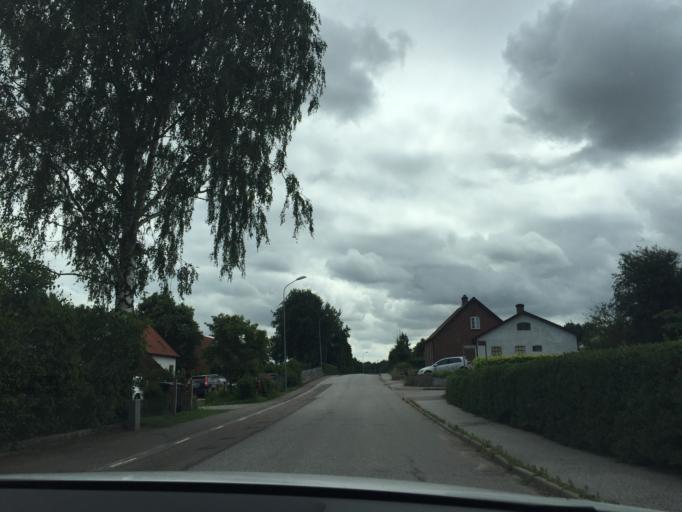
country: SE
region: Skane
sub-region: Sjobo Kommun
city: Blentarp
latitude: 55.5890
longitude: 13.5997
